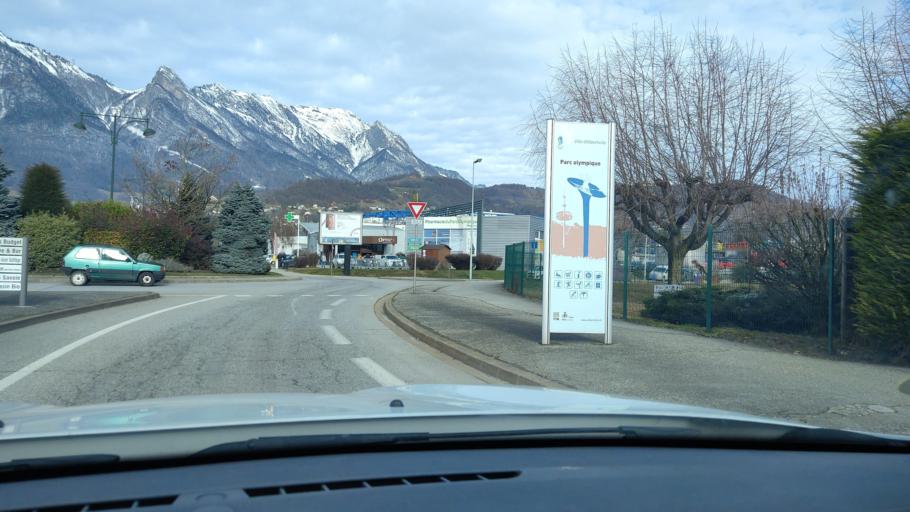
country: FR
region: Rhone-Alpes
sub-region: Departement de la Savoie
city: Grignon
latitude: 45.6609
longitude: 6.3739
